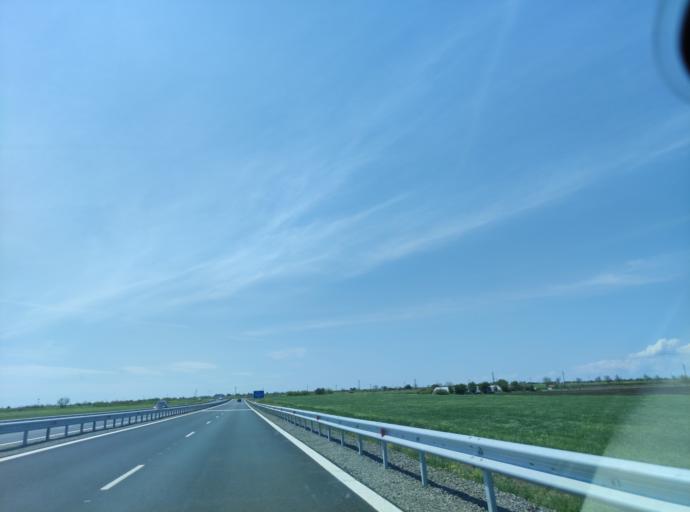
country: BG
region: Burgas
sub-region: Obshtina Pomorie
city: Pomorie
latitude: 42.5898
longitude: 27.6033
